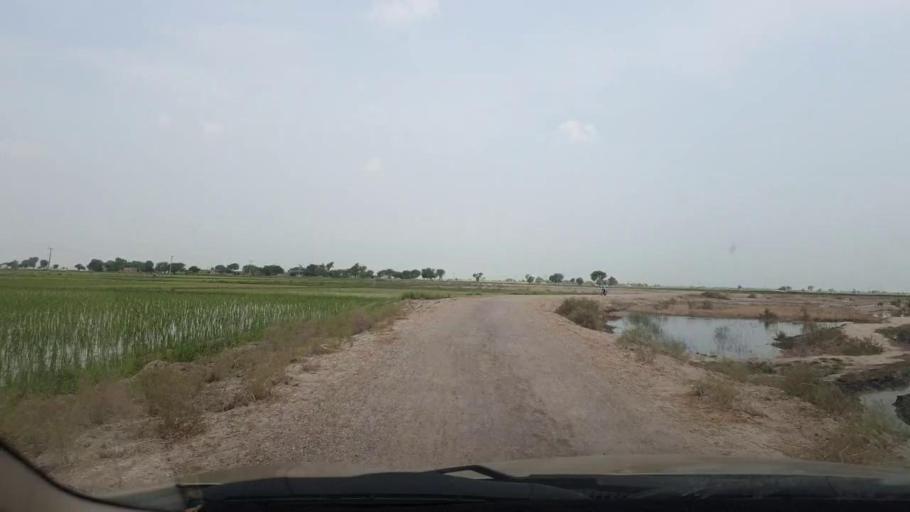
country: PK
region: Sindh
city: Larkana
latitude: 27.5146
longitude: 68.1300
